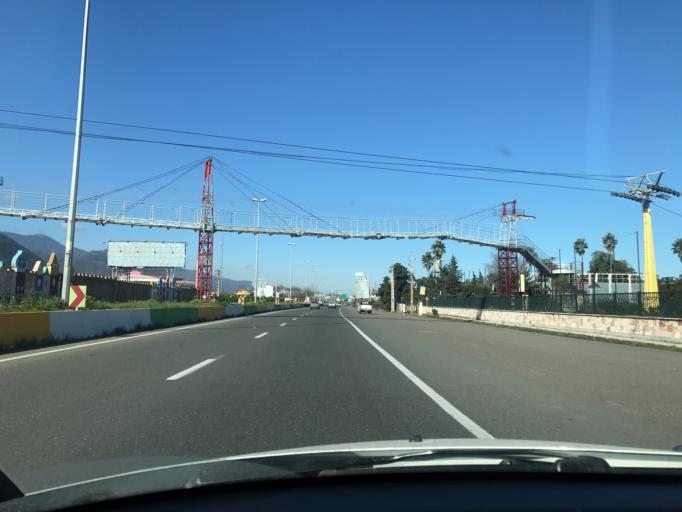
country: IR
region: Mazandaran
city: Ramsar
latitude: 36.9599
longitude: 50.6008
